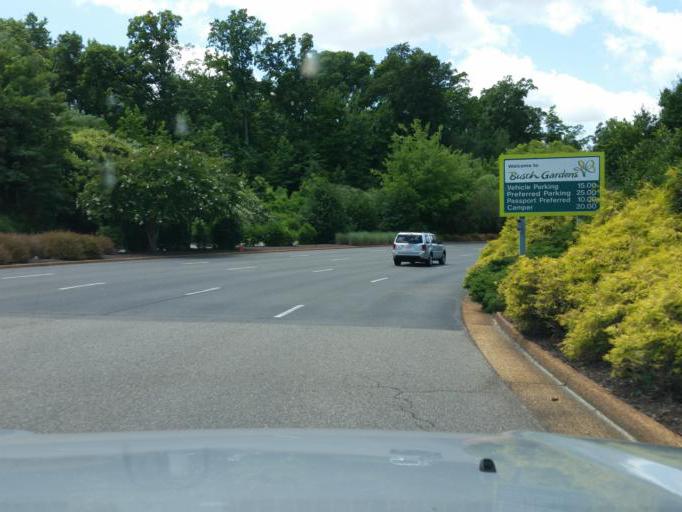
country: US
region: Virginia
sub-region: City of Williamsburg
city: Williamsburg
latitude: 37.2344
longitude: -76.6373
